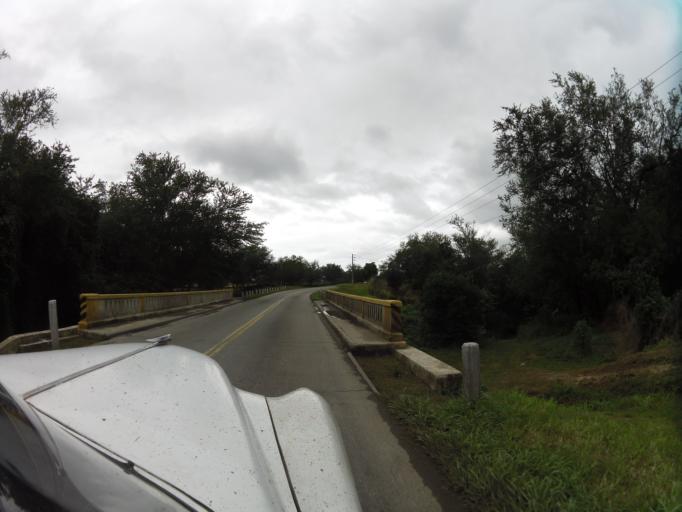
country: CU
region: Las Tunas
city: Las Tunas
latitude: 20.9198
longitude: -76.8907
